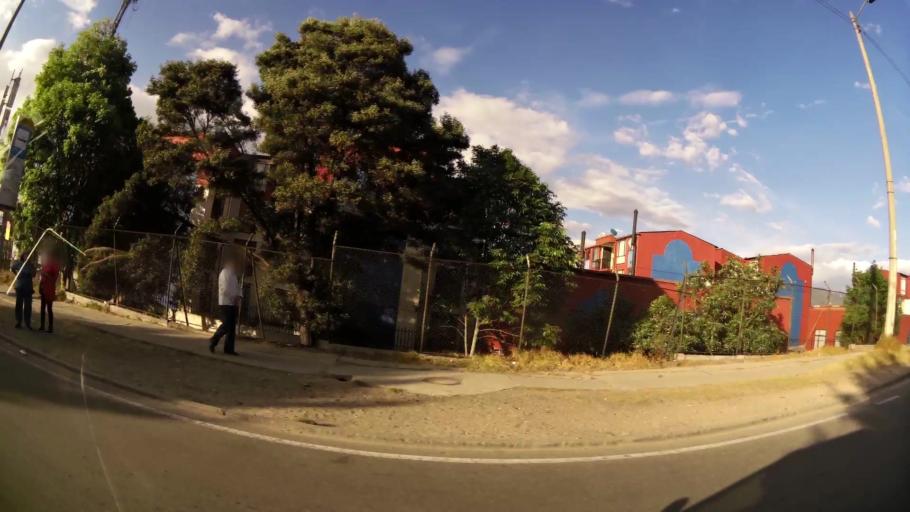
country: CO
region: Cundinamarca
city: Soacha
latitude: 4.5685
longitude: -74.1455
